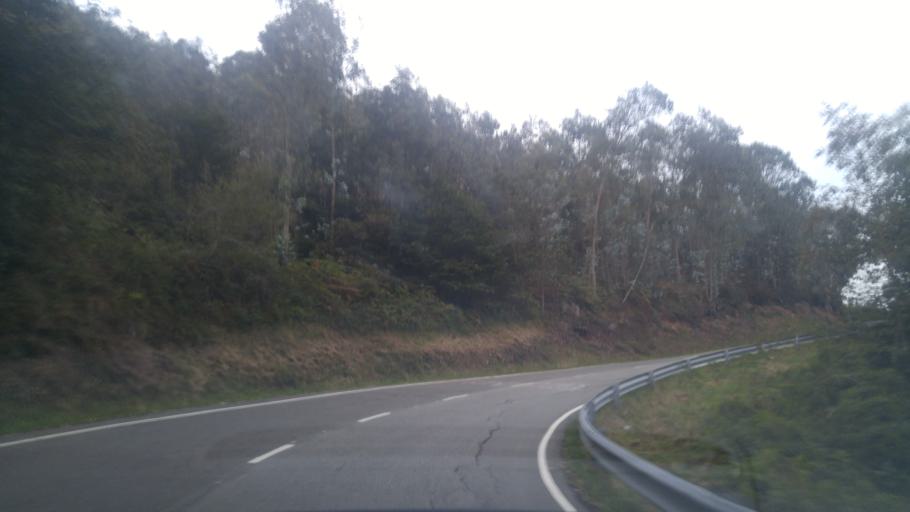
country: ES
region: Asturias
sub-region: Province of Asturias
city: Oviedo
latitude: 43.3847
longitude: -5.8509
